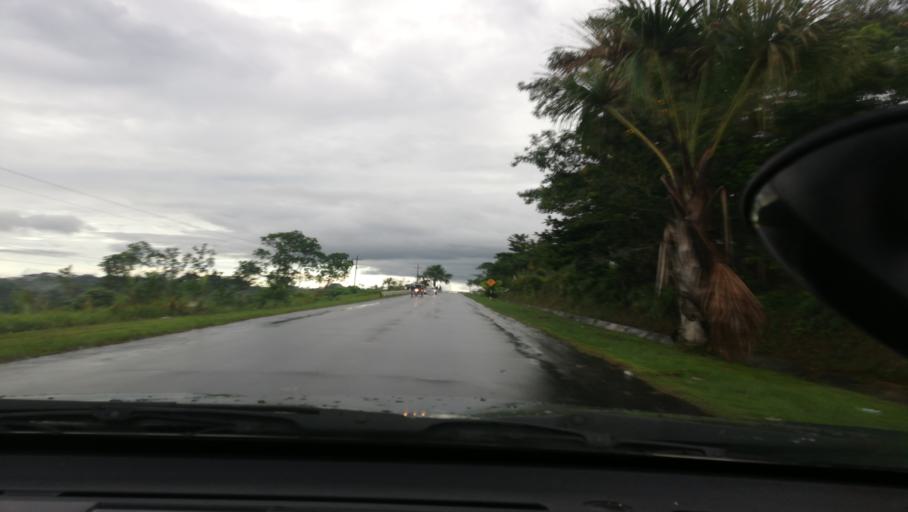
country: PE
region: Loreto
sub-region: Provincia de Maynas
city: Iquitos
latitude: -3.8978
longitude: -73.3490
